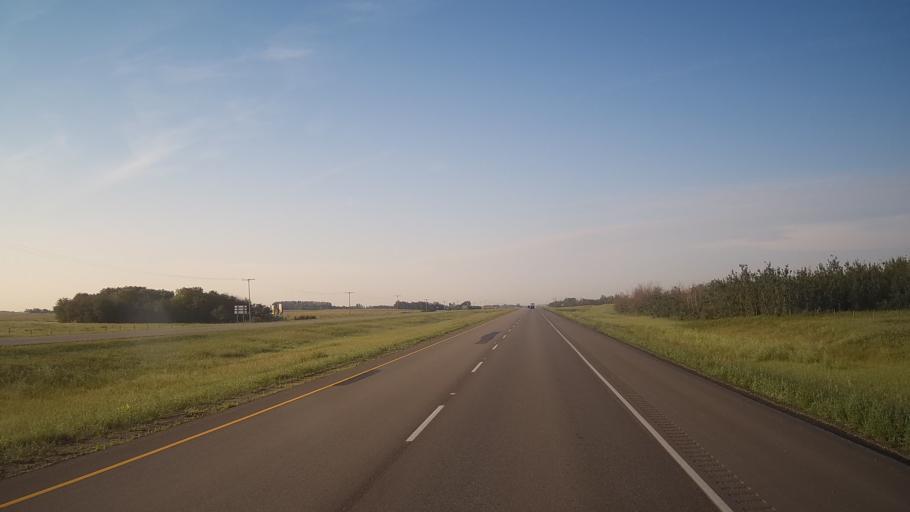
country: CA
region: Saskatchewan
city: Saskatoon
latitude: 52.0420
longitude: -106.5908
